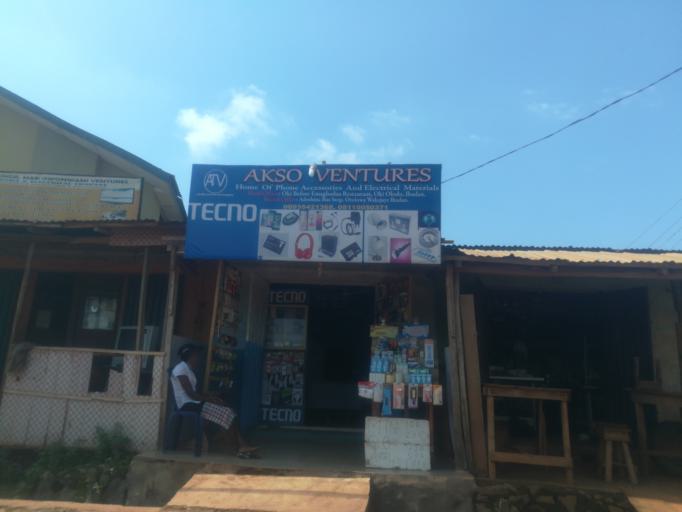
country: NG
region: Oyo
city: Egbeda
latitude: 7.4159
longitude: 3.9905
